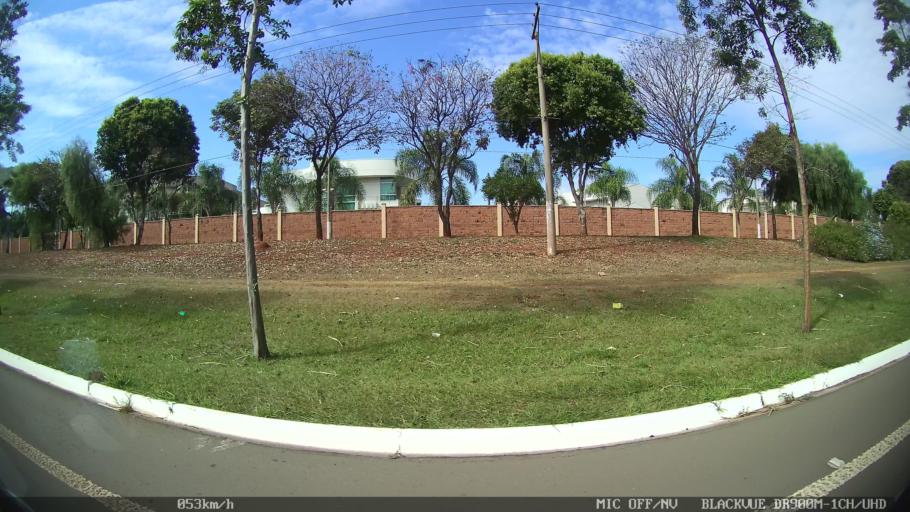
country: BR
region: Sao Paulo
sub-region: Santa Barbara D'Oeste
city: Santa Barbara d'Oeste
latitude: -22.7593
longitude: -47.4319
